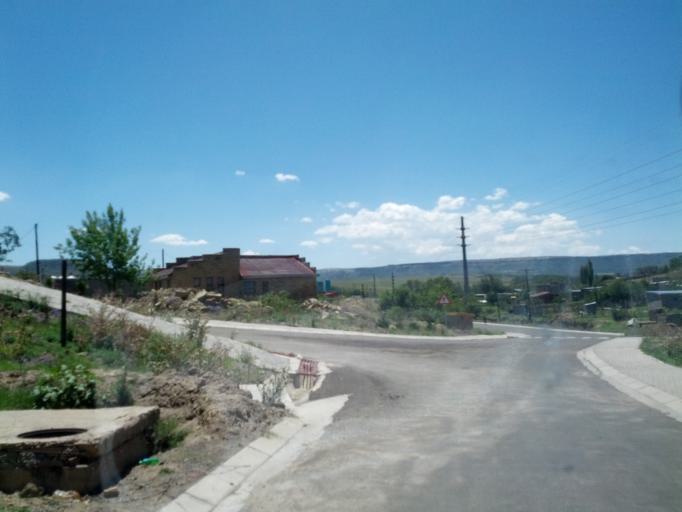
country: LS
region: Maseru
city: Maseru
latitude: -29.3065
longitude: 27.4898
